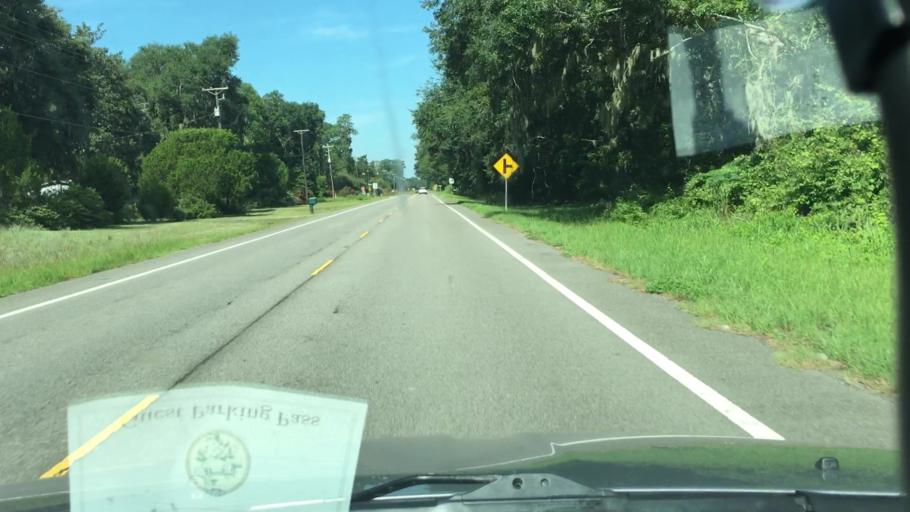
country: US
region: South Carolina
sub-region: Beaufort County
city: Beaufort
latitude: 32.4135
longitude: -80.5042
